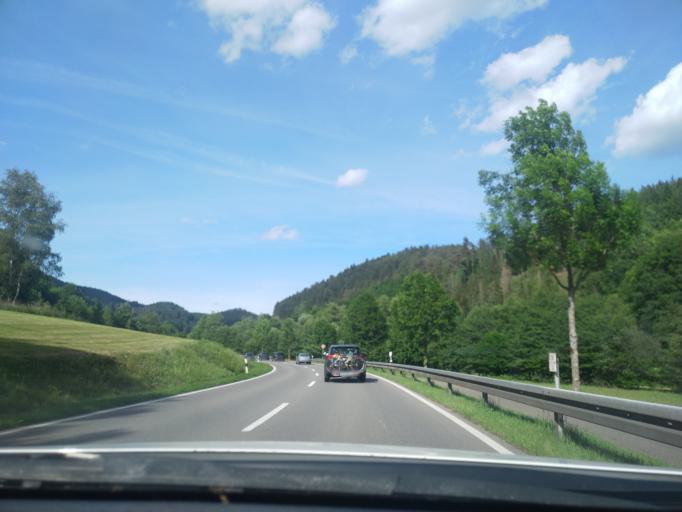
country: DE
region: Baden-Wuerttemberg
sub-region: Freiburg Region
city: Schenkenzell
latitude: 48.3037
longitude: 8.3676
